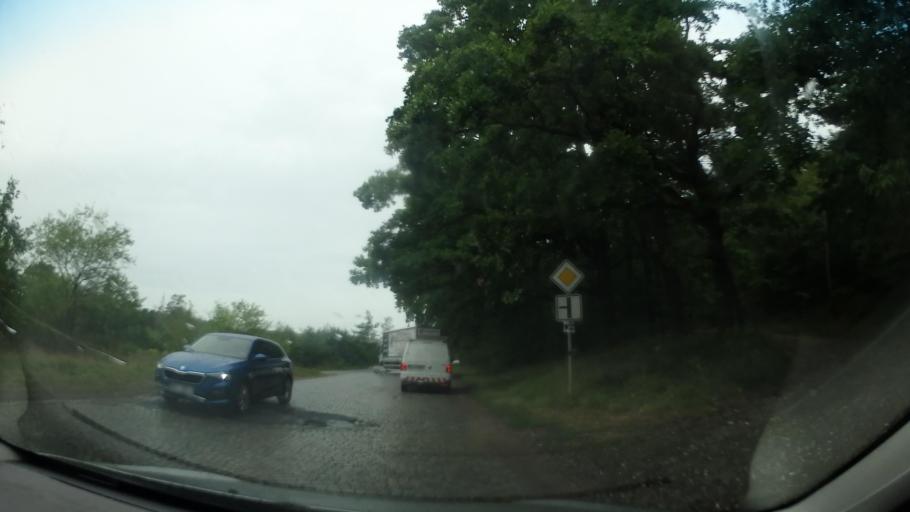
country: CZ
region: Central Bohemia
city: Milovice
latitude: 50.2481
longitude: 14.9209
